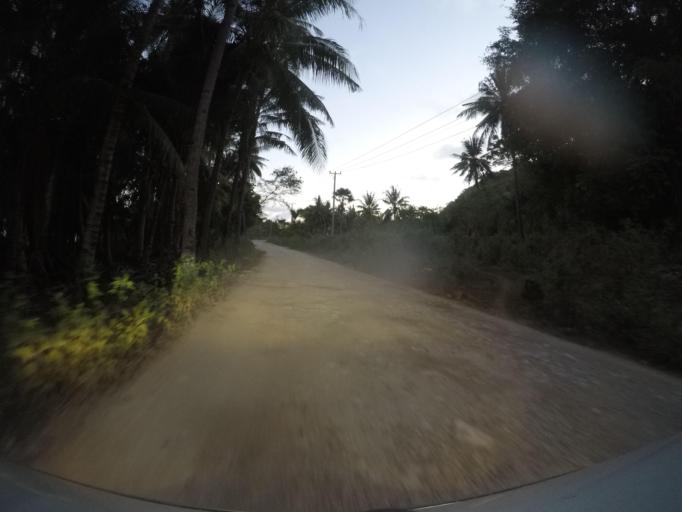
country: TL
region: Viqueque
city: Viqueque
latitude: -8.7943
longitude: 126.6239
